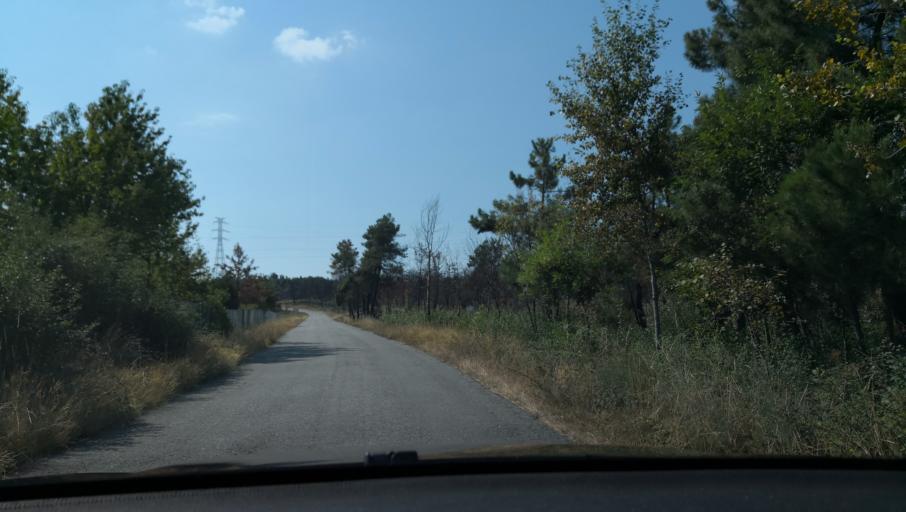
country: PT
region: Vila Real
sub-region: Sabrosa
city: Sabrosa
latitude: 41.3299
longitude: -7.6151
